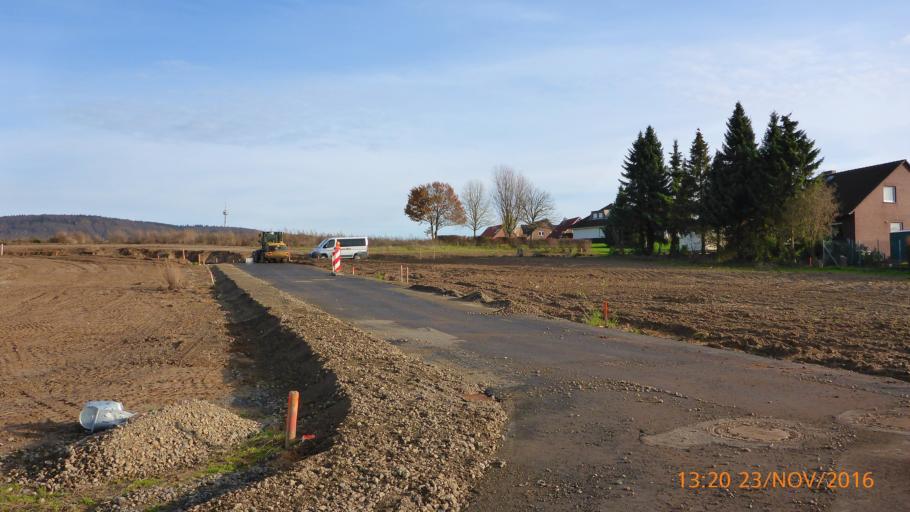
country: DE
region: Lower Saxony
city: Lauenau
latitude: 52.2798
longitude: 9.3726
